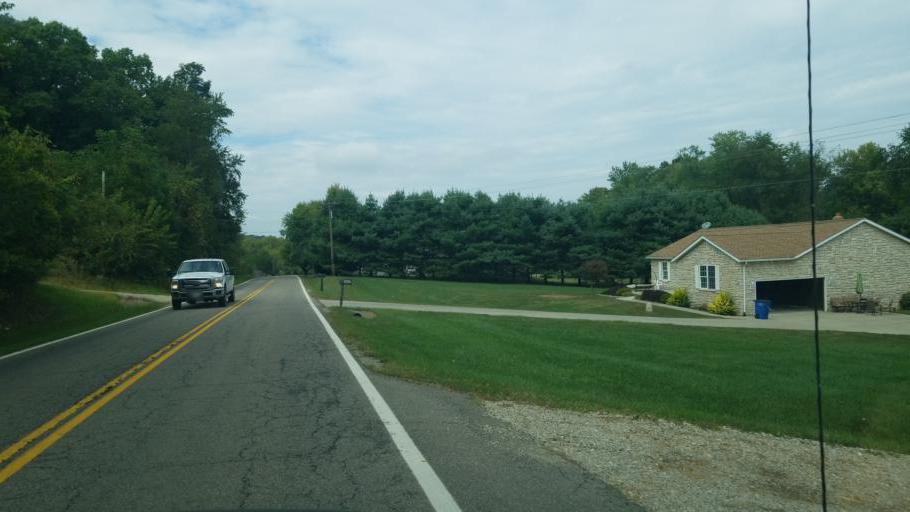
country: US
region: Ohio
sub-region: Licking County
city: Newark
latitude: 39.9997
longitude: -82.2807
